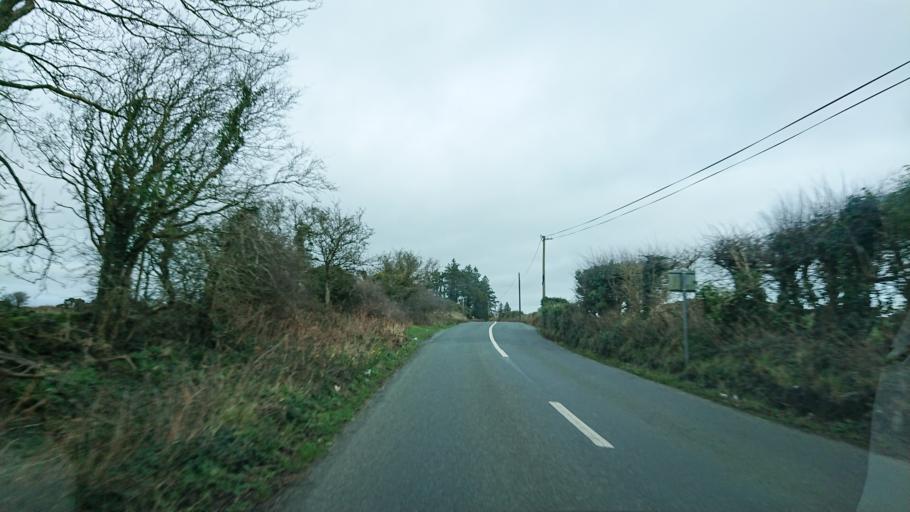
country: IE
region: Leinster
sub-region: Kilkenny
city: Mooncoin
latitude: 52.1963
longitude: -7.2713
